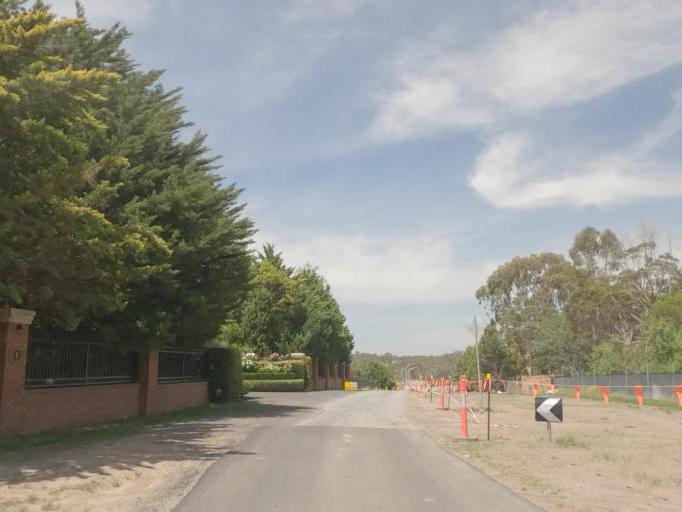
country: AU
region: Victoria
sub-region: Hume
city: Greenvale
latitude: -37.6391
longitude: 144.8751
